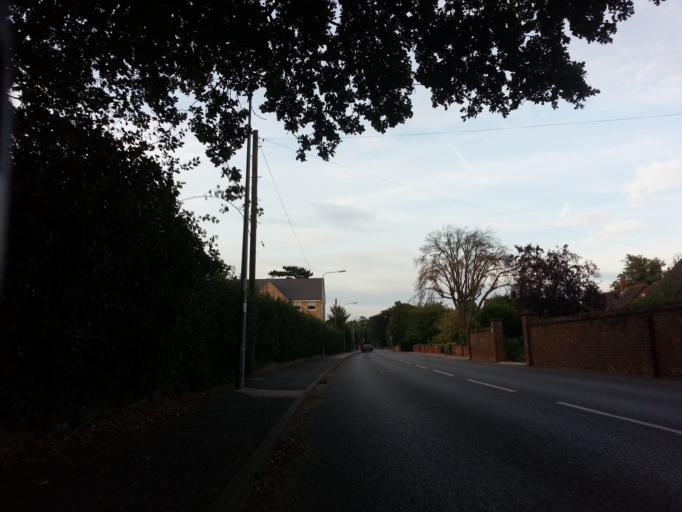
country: GB
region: England
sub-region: Suffolk
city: Ipswich
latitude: 52.0453
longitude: 1.1397
